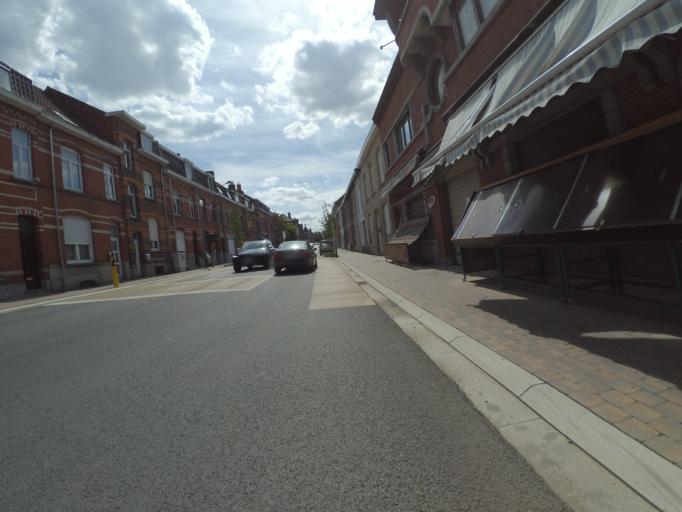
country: BE
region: Flanders
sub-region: Provincie Oost-Vlaanderen
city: Ronse
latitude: 50.7465
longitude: 3.6067
